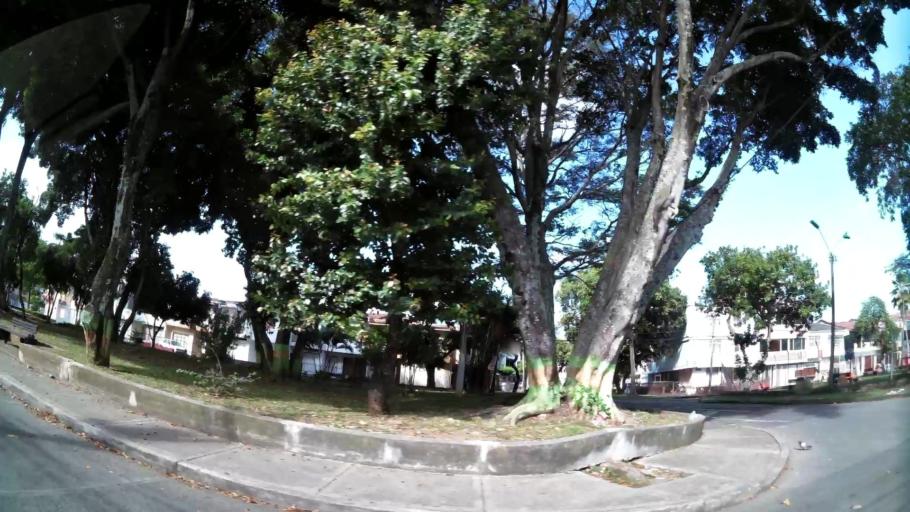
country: CO
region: Valle del Cauca
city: Cali
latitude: 3.4317
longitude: -76.5339
